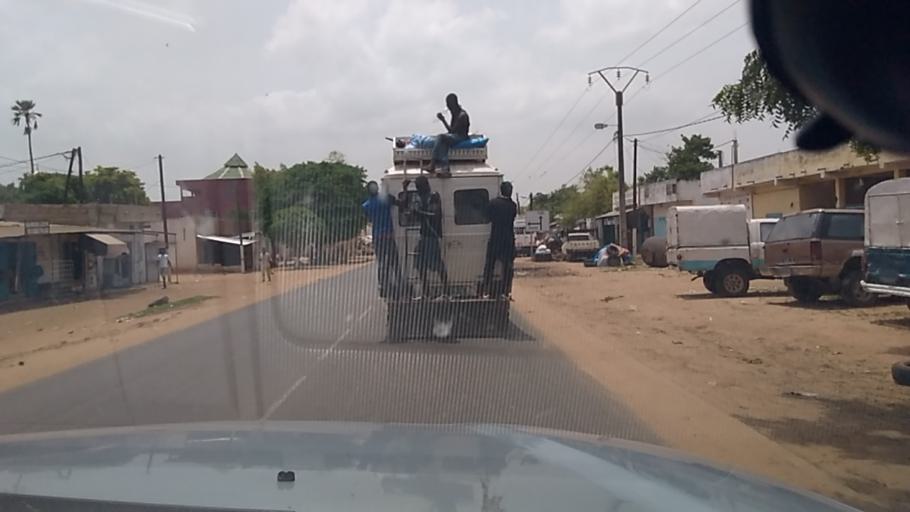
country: SN
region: Thies
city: Mekhe
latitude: 15.0150
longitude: -16.7398
